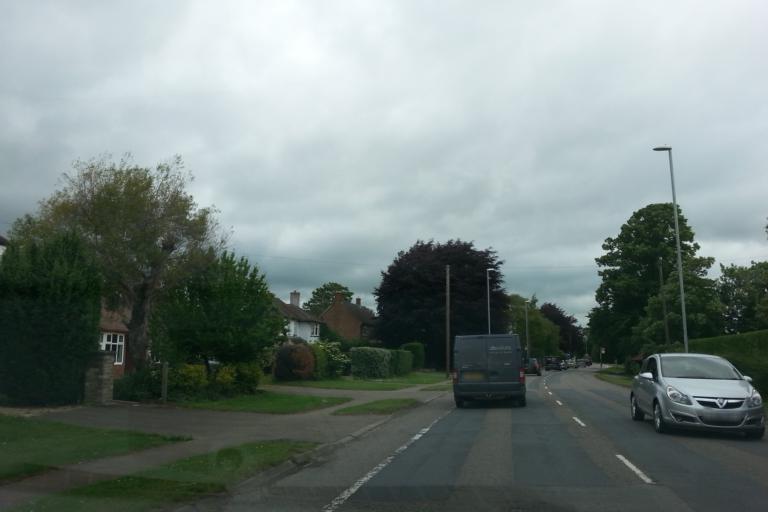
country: GB
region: England
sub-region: Cambridgeshire
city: Cambridge
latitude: 52.1573
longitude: 0.1282
